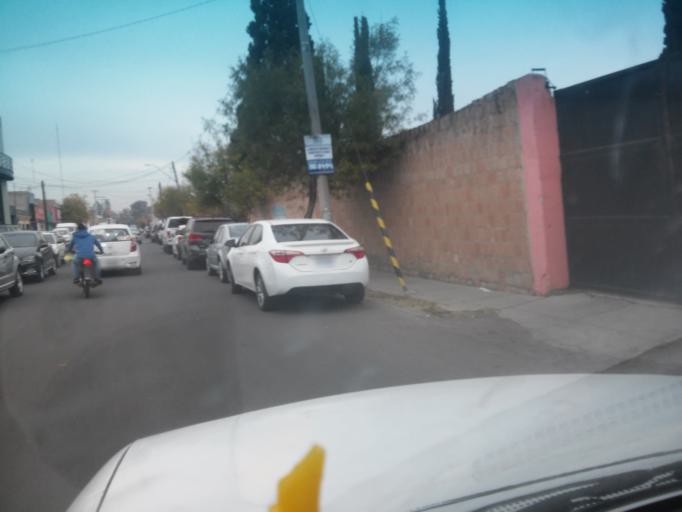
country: MX
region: Durango
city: Victoria de Durango
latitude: 24.0123
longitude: -104.6780
